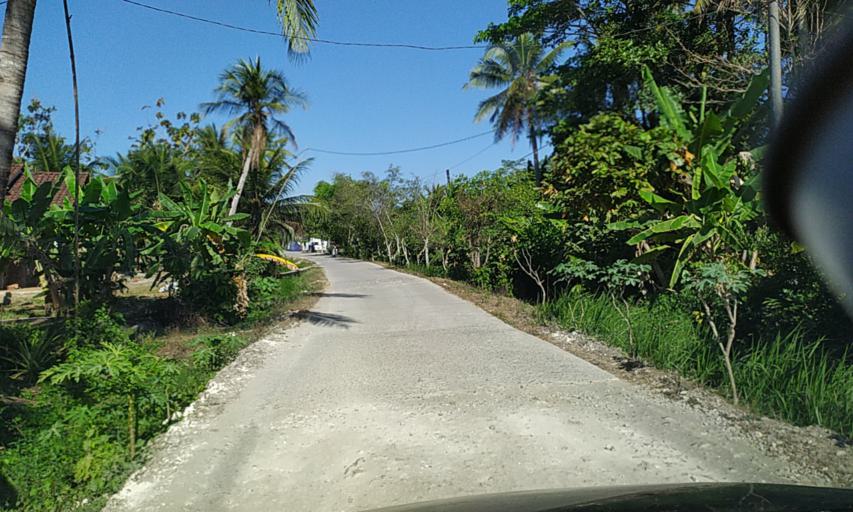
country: ID
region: Central Java
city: Kalenaren
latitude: -7.5826
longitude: 108.7926
